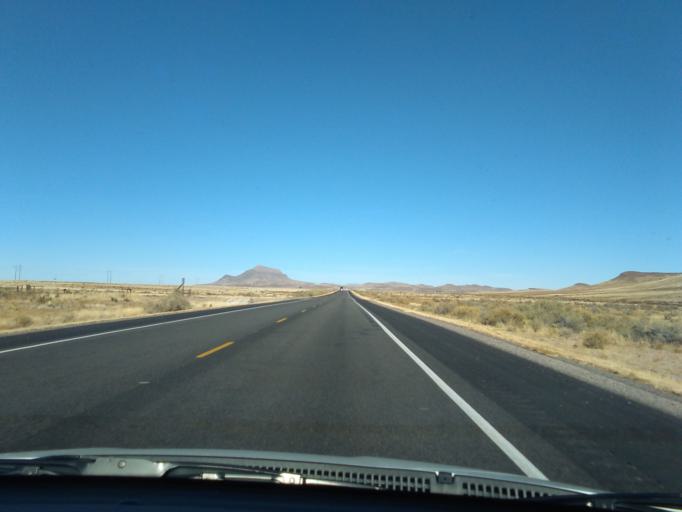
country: US
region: New Mexico
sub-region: Dona Ana County
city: Hatch
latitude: 32.5358
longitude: -107.4862
